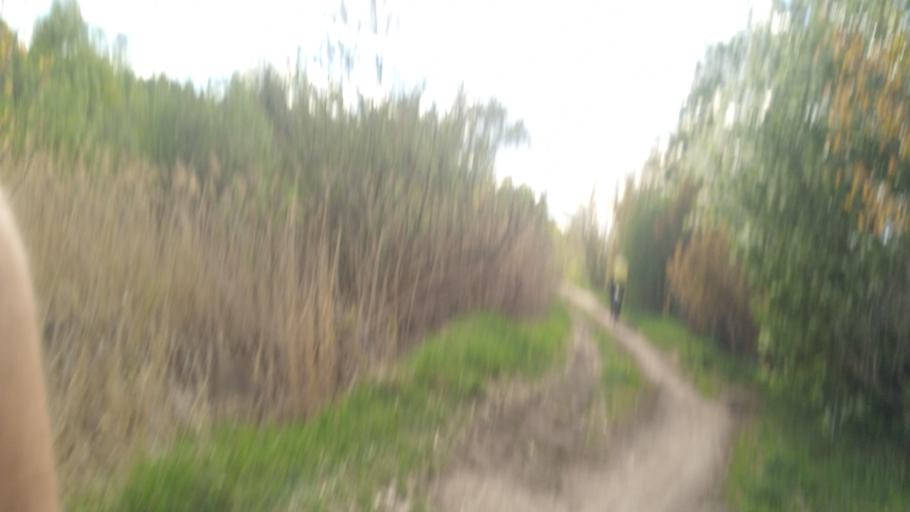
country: RU
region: Chelyabinsk
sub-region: Gorod Chelyabinsk
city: Chelyabinsk
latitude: 55.1688
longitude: 61.3325
